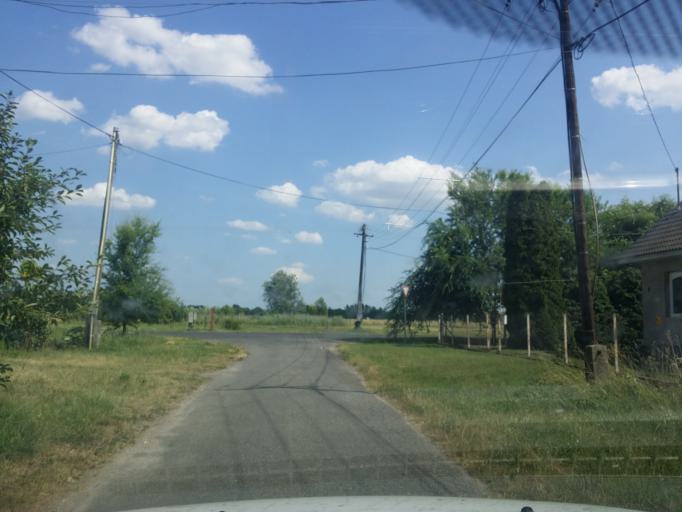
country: HU
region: Bacs-Kiskun
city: Jaszszentlaszlo
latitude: 46.5709
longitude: 19.7658
